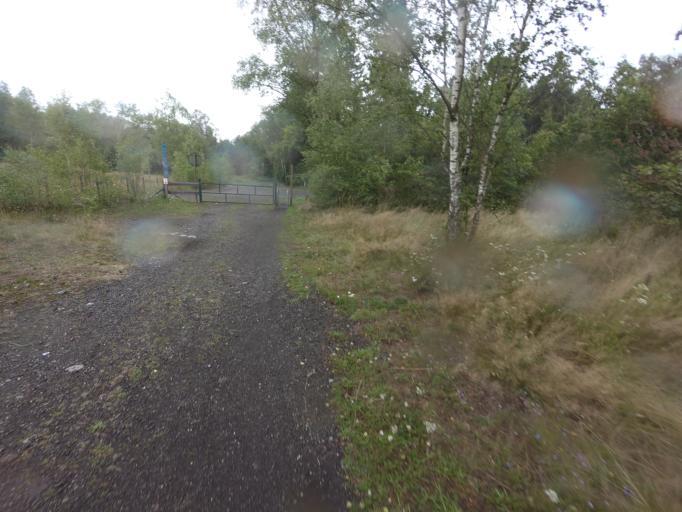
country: BE
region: Wallonia
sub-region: Province de Liege
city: Plombieres
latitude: 50.7348
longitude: 5.9647
